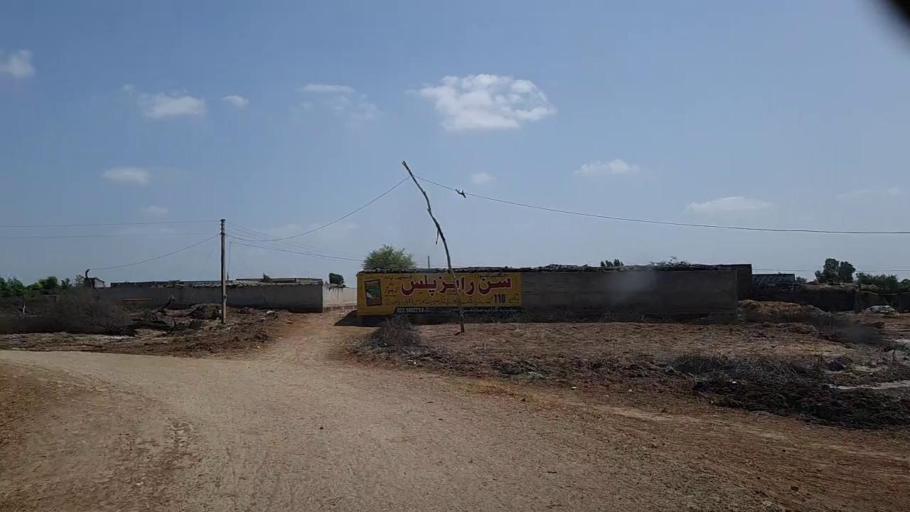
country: PK
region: Sindh
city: Kario
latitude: 24.6408
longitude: 68.5686
